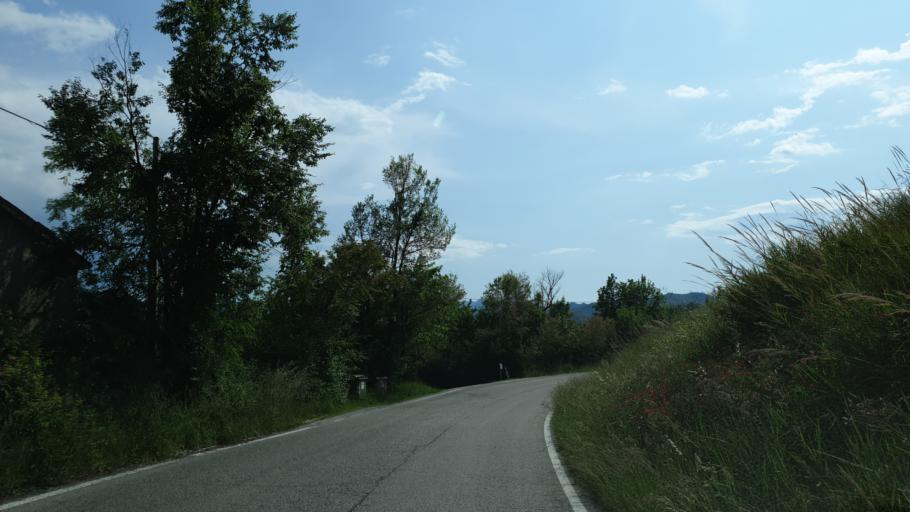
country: IT
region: Emilia-Romagna
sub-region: Forli-Cesena
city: Sarsina
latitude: 43.9092
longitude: 12.1884
